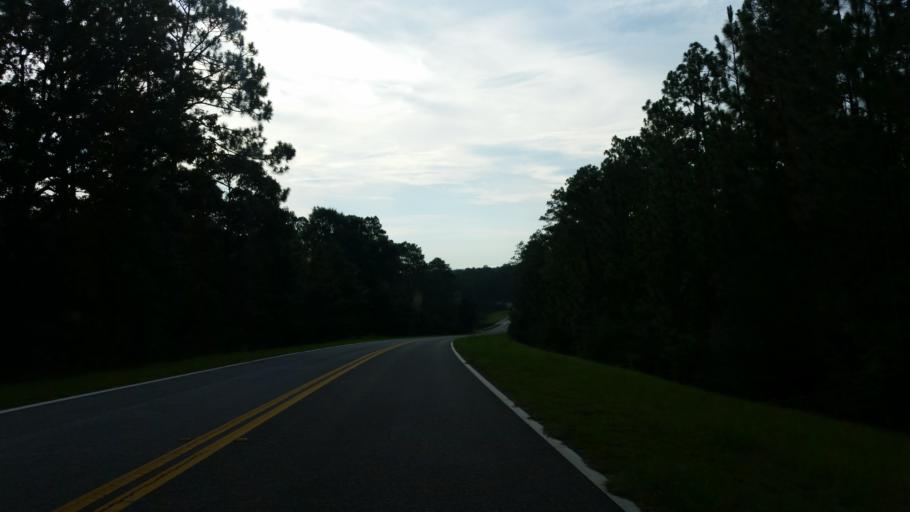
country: US
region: Florida
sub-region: Escambia County
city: Molino
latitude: 30.7708
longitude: -87.5085
